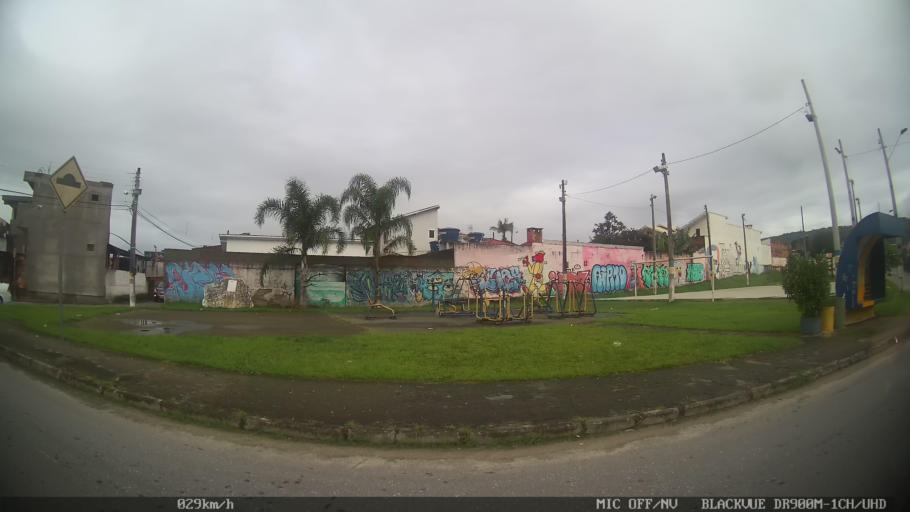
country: BR
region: Santa Catarina
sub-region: Biguacu
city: Biguacu
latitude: -27.5307
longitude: -48.6405
